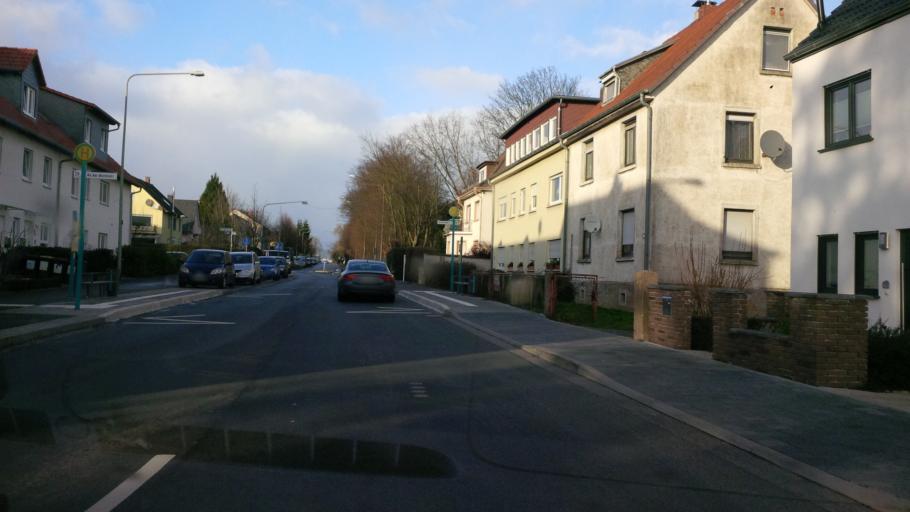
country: DE
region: Hesse
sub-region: Regierungsbezirk Darmstadt
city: Bad Homburg vor der Hoehe
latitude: 50.1971
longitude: 8.6665
